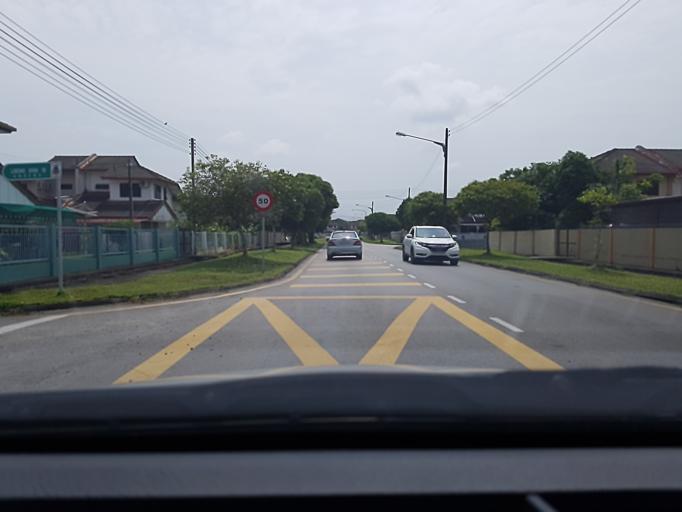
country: MY
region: Sarawak
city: Kuching
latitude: 1.5151
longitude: 110.3626
